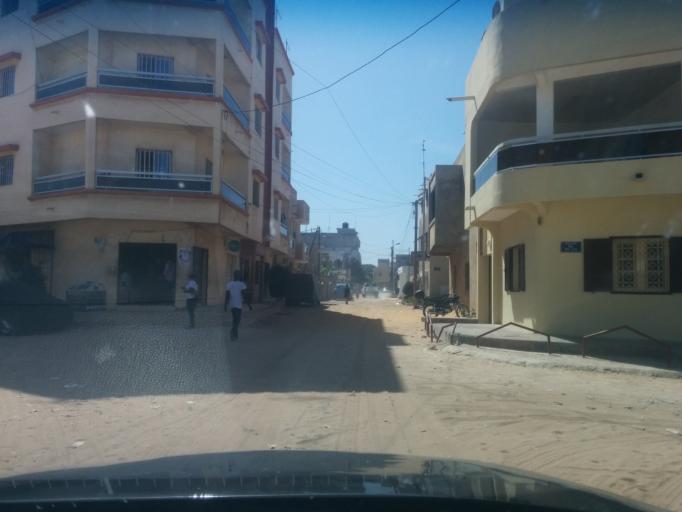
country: SN
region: Dakar
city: Grand Dakar
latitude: 14.7491
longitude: -17.4420
